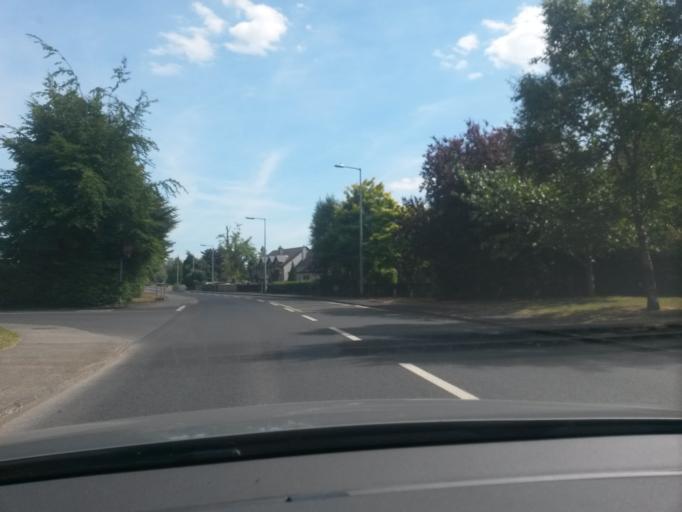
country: IE
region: Leinster
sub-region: Kildare
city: Naas
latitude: 53.2175
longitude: -6.6554
